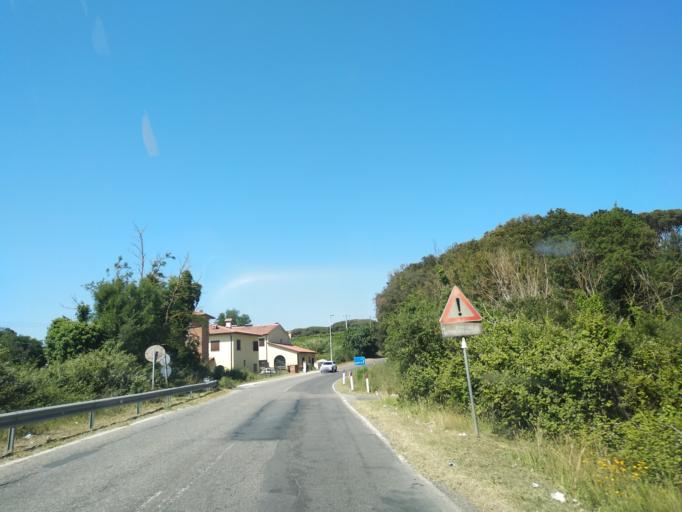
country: IT
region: Tuscany
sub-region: Provincia di Livorno
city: Livorno
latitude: 43.5672
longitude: 10.3611
